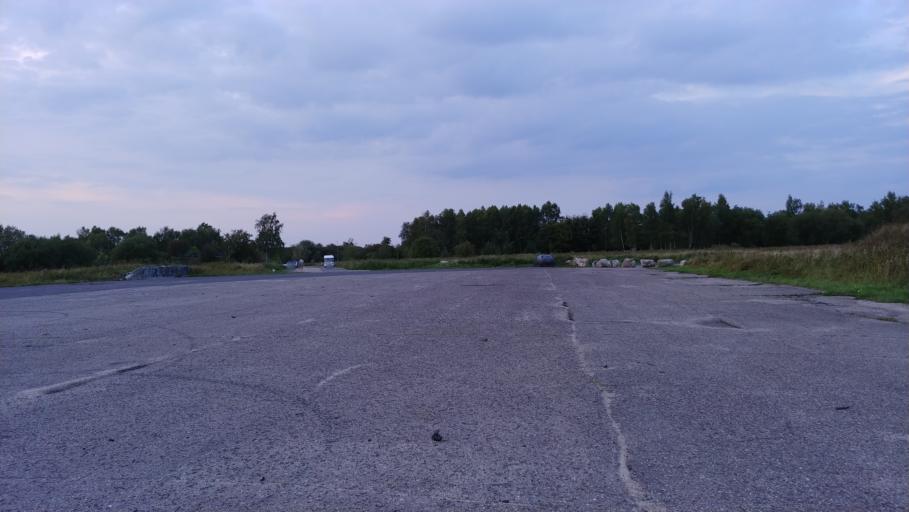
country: PL
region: West Pomeranian Voivodeship
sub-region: Powiat kolobrzeski
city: Kolobrzeg
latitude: 54.1961
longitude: 15.6641
